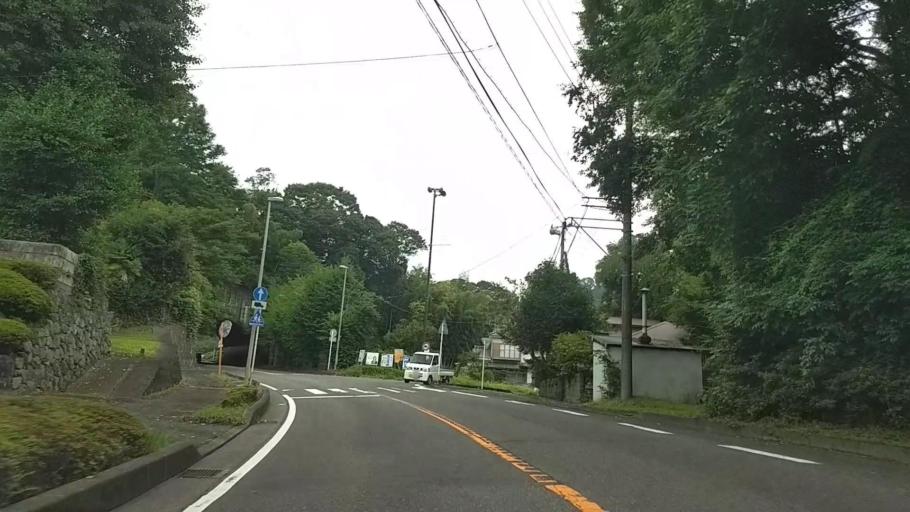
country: JP
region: Kanagawa
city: Hadano
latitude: 35.3369
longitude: 139.1980
